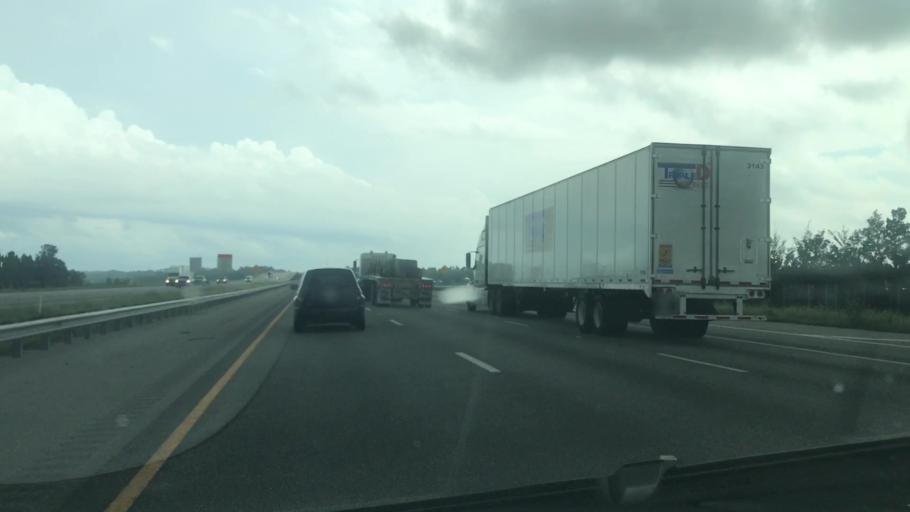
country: US
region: Georgia
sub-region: Glynn County
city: Dock Junction
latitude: 31.1994
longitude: -81.5375
